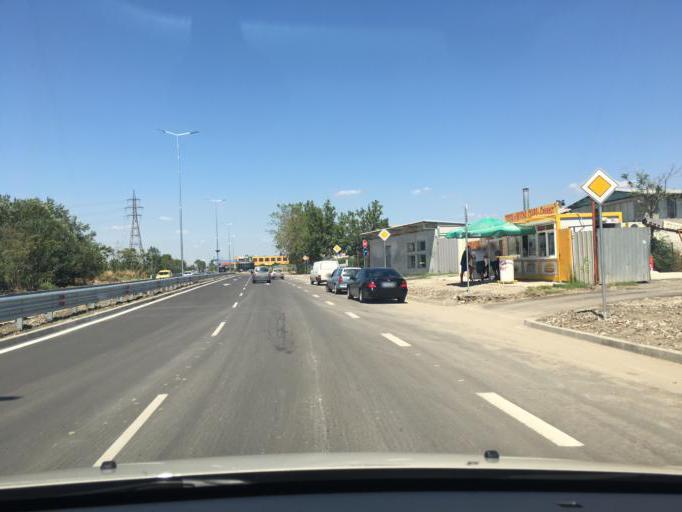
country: BG
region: Burgas
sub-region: Obshtina Burgas
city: Burgas
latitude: 42.5008
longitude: 27.4542
